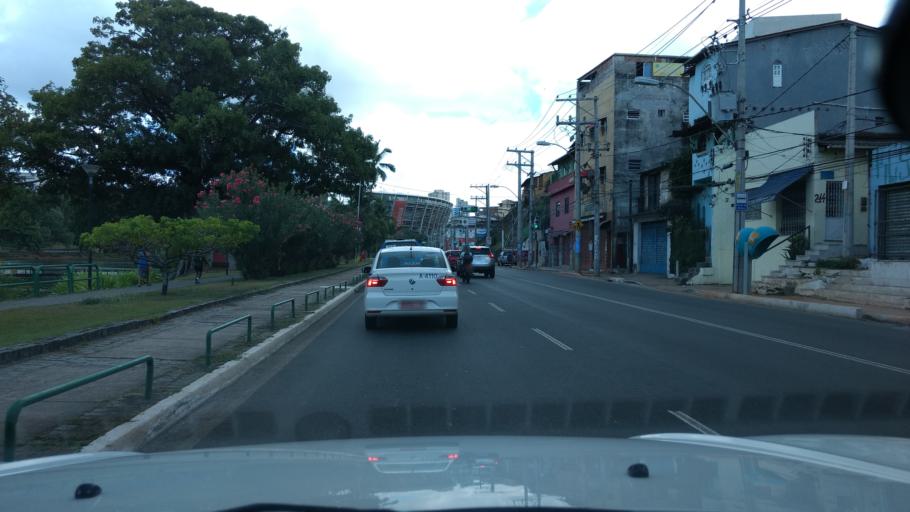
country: BR
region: Bahia
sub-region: Salvador
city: Salvador
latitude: -12.9843
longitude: -38.5039
